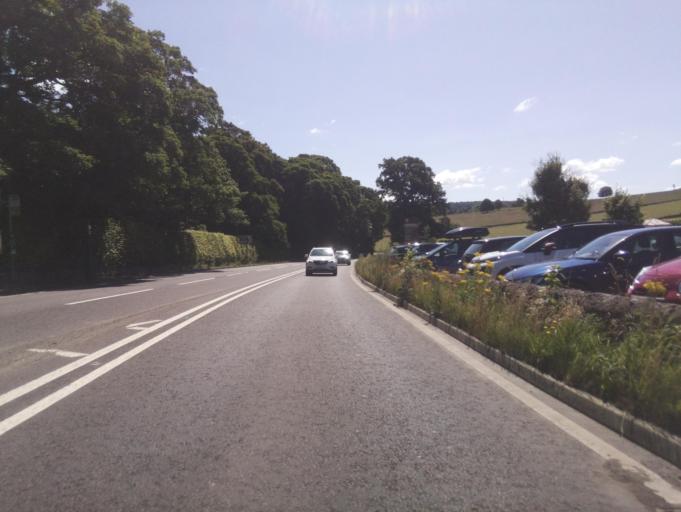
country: GB
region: England
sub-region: Derbyshire
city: Bakewell
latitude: 53.1919
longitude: -1.6514
